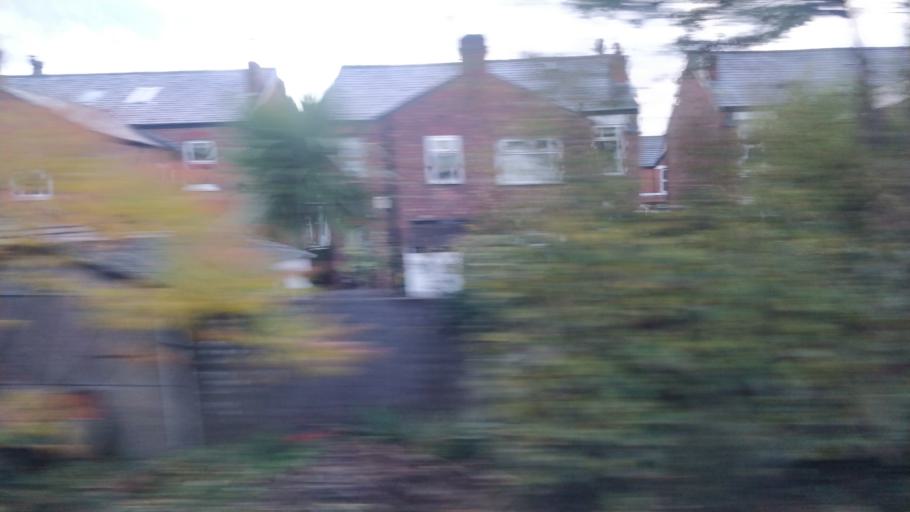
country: GB
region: England
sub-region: Sefton
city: Southport
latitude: 53.6445
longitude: -2.9737
